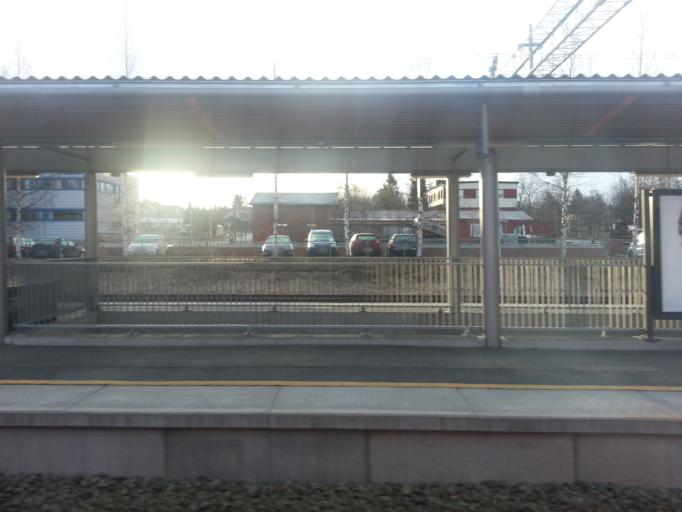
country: NO
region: Sor-Trondelag
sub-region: Trondheim
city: Trondheim
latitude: 63.3510
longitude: 10.3578
